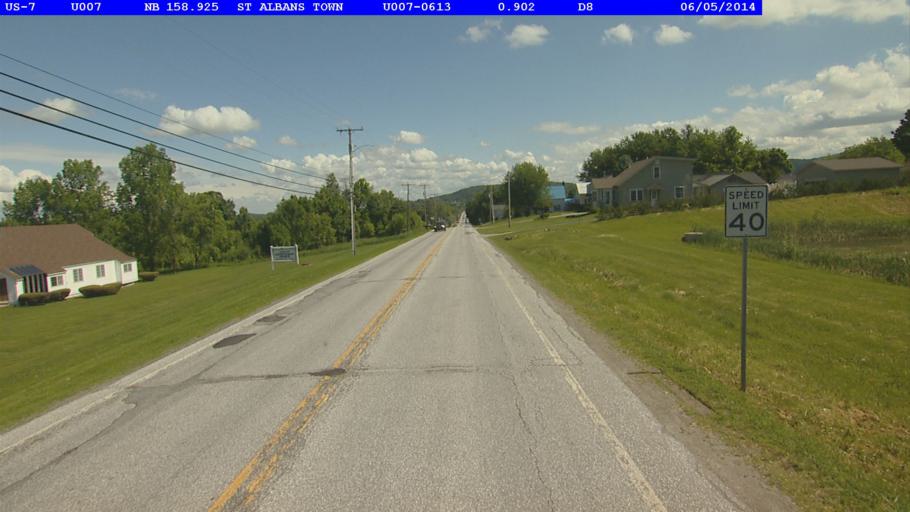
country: US
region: Vermont
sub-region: Franklin County
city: Saint Albans
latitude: 44.7919
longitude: -73.0966
